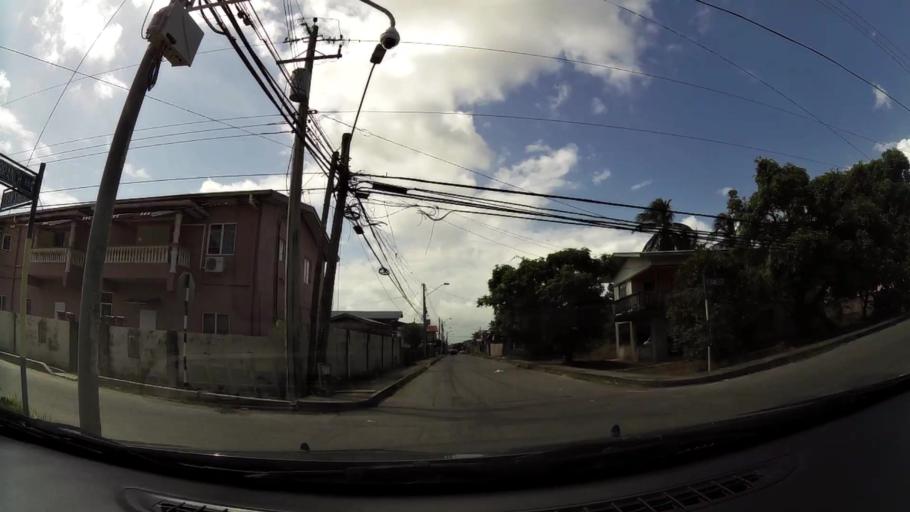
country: TT
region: Borough of Arima
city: Arima
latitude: 10.6309
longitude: -61.2778
